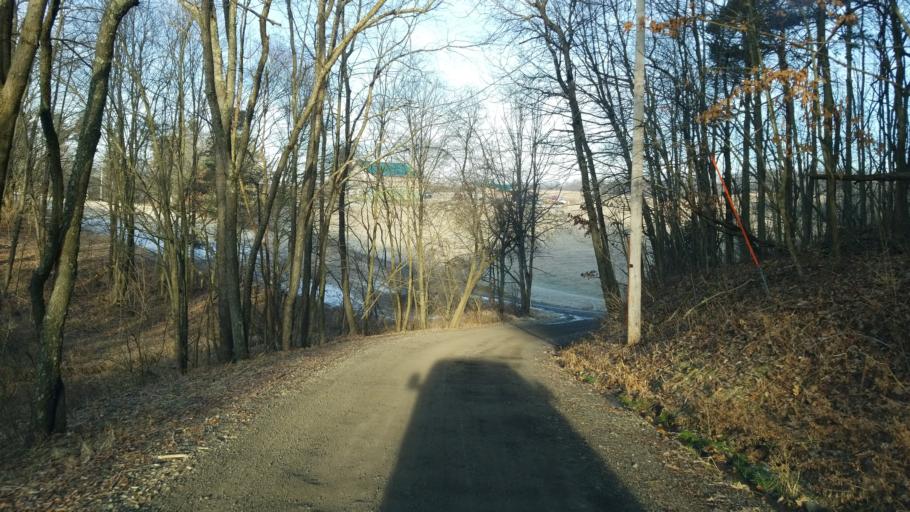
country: US
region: Pennsylvania
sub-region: Indiana County
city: Chevy Chase Heights
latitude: 40.8500
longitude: -79.2633
